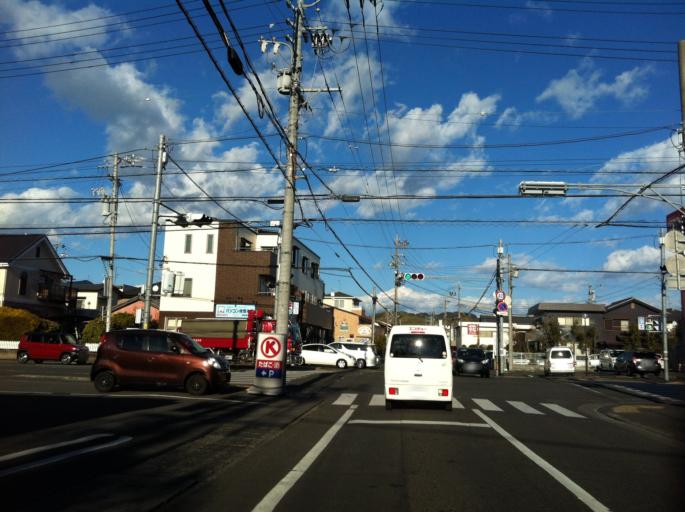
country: JP
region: Shizuoka
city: Shizuoka-shi
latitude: 35.0021
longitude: 138.3911
